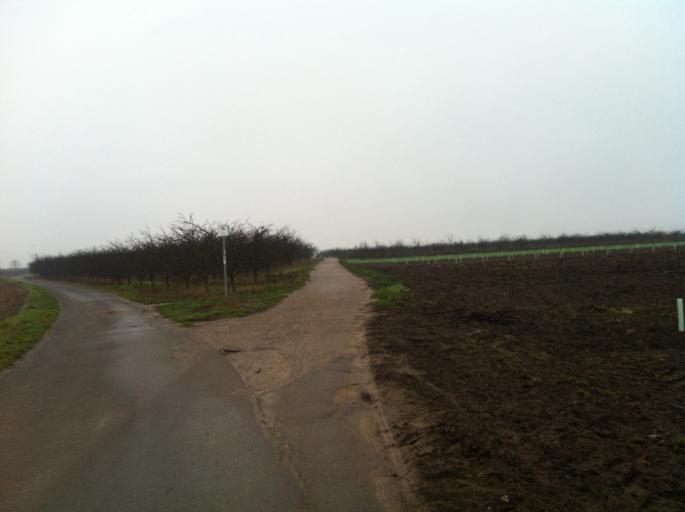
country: DE
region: Rheinland-Pfalz
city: Budenheim
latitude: 49.9889
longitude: 8.1577
